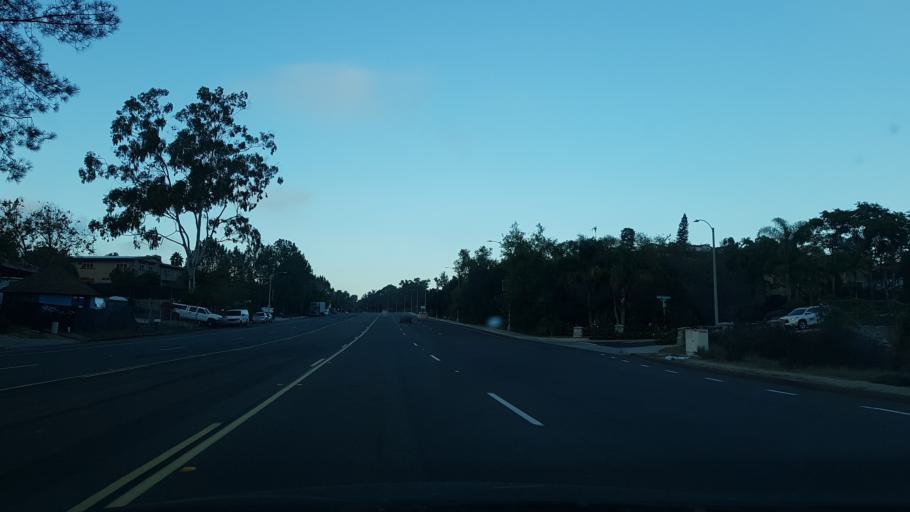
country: US
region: California
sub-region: San Diego County
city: Encinitas
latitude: 33.0262
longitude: -117.2555
